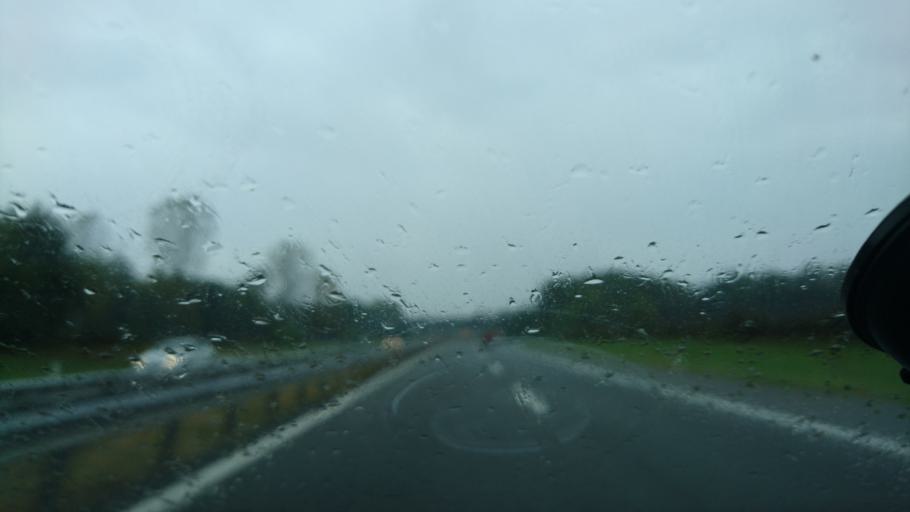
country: IT
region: Piedmont
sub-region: Provincia di Novara
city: Fontaneto D'Agogna
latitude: 45.6408
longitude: 8.4590
